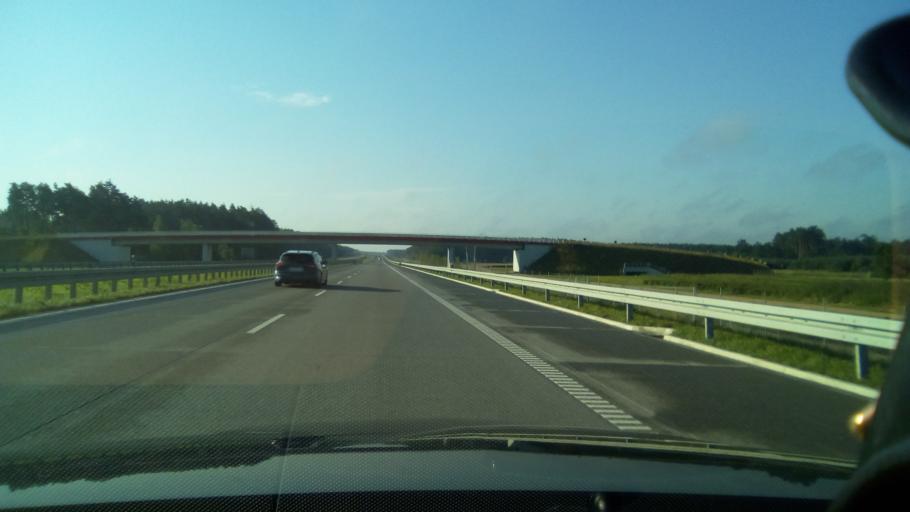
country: PL
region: Silesian Voivodeship
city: Wozniki
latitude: 50.5575
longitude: 19.0584
